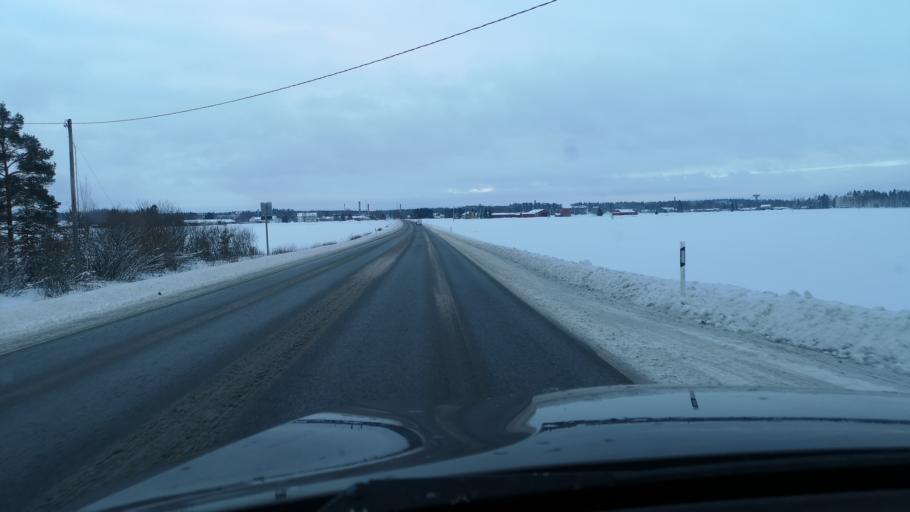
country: FI
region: Varsinais-Suomi
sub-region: Loimaa
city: Loimaa
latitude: 60.8671
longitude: 23.0553
